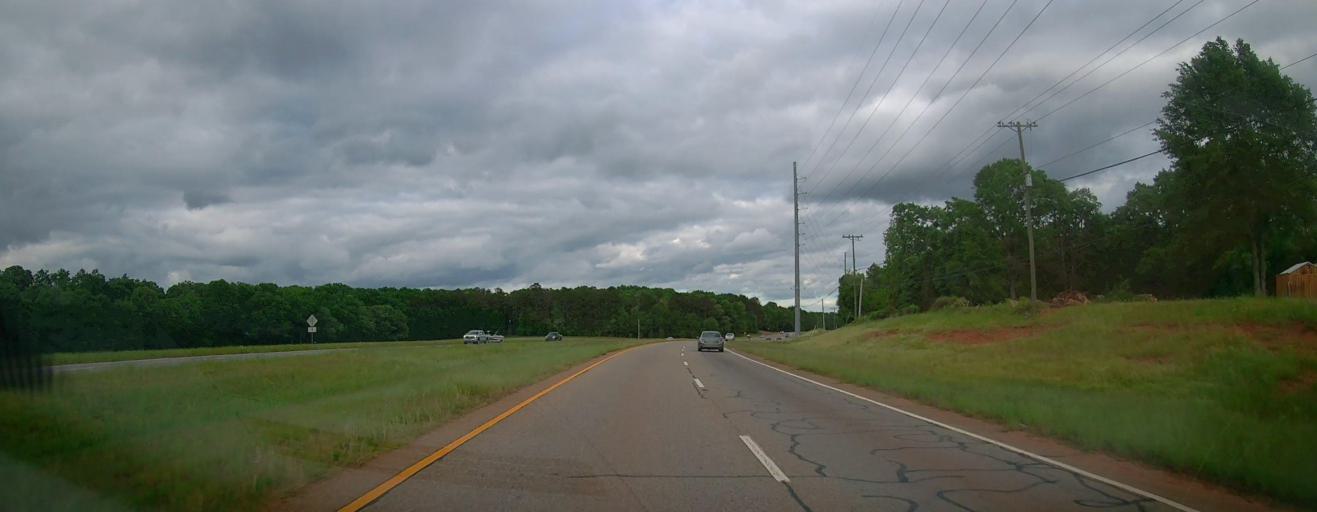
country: US
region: Georgia
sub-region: Oconee County
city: Bogart
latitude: 33.9172
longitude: -83.5490
